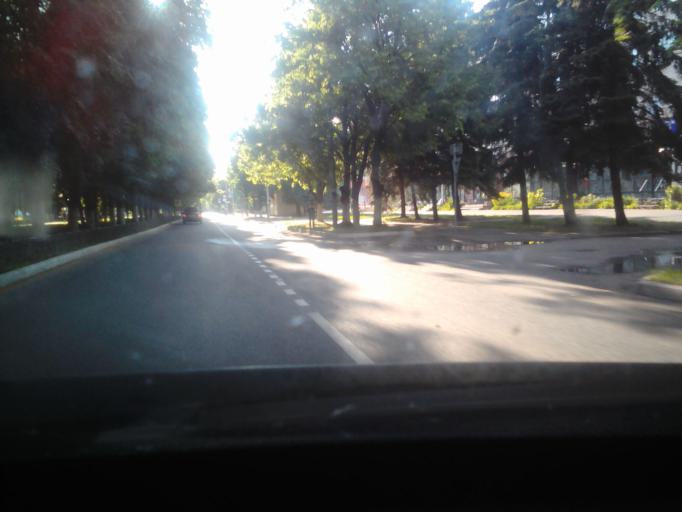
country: RU
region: Kursk
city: Kurchatov
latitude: 51.6605
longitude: 35.6534
